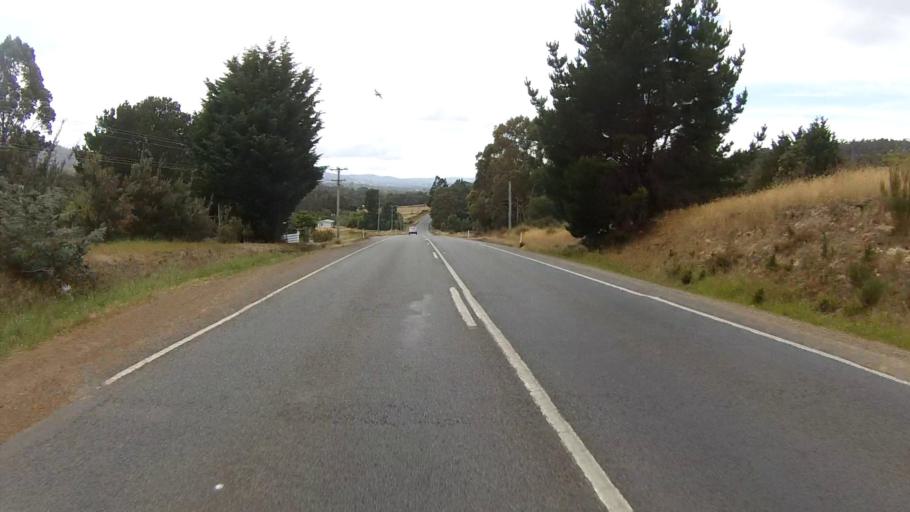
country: AU
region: Tasmania
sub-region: Kingborough
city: Kettering
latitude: -43.0891
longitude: 147.2505
